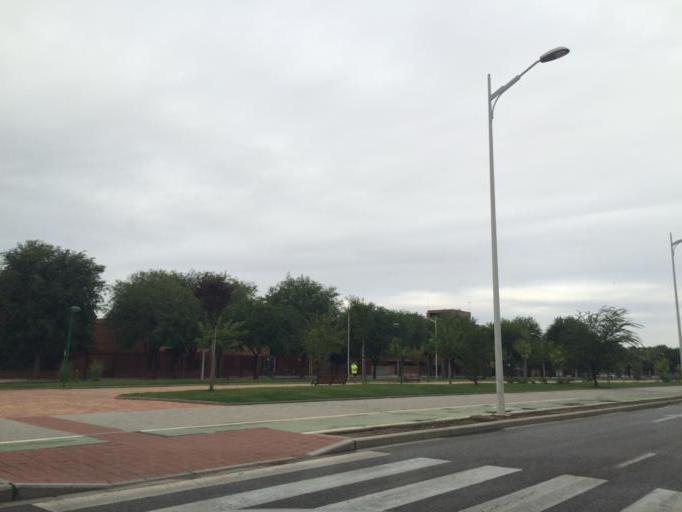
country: ES
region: Castille-La Mancha
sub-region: Provincia de Albacete
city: Albacete
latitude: 39.0058
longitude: -1.8597
